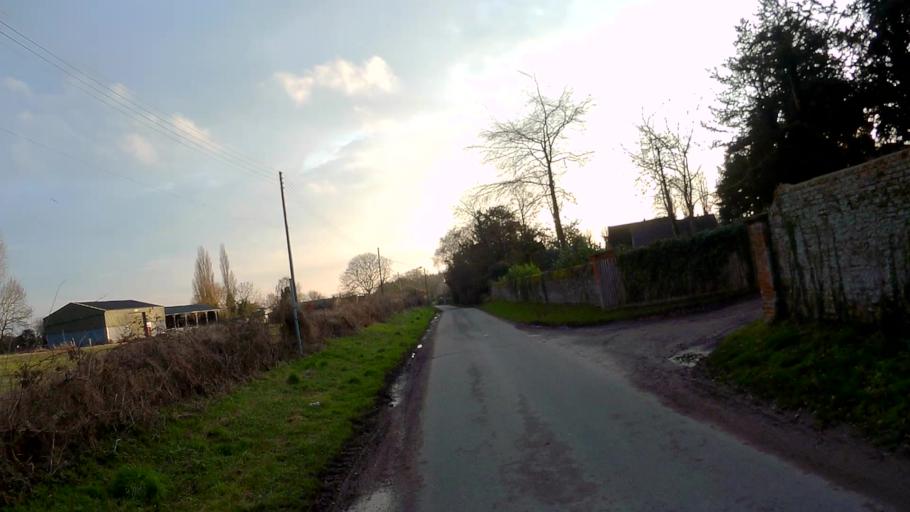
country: GB
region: England
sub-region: Lincolnshire
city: Bourne
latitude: 52.8050
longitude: -0.3928
